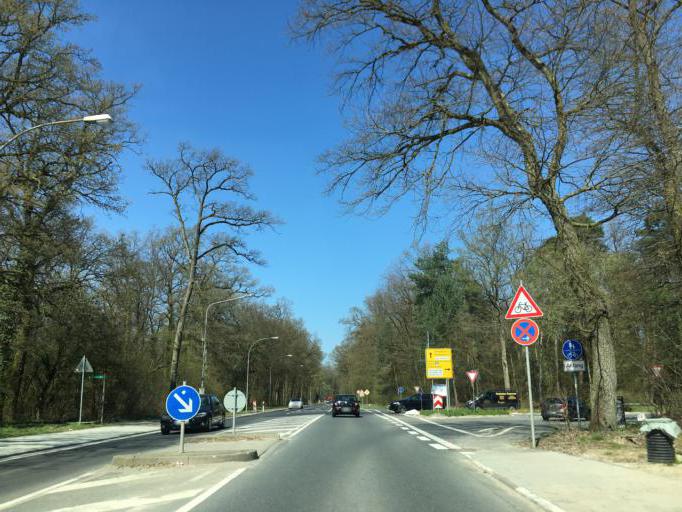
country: DE
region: Hesse
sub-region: Regierungsbezirk Darmstadt
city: Muehlheim am Main
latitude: 50.1025
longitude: 8.8493
